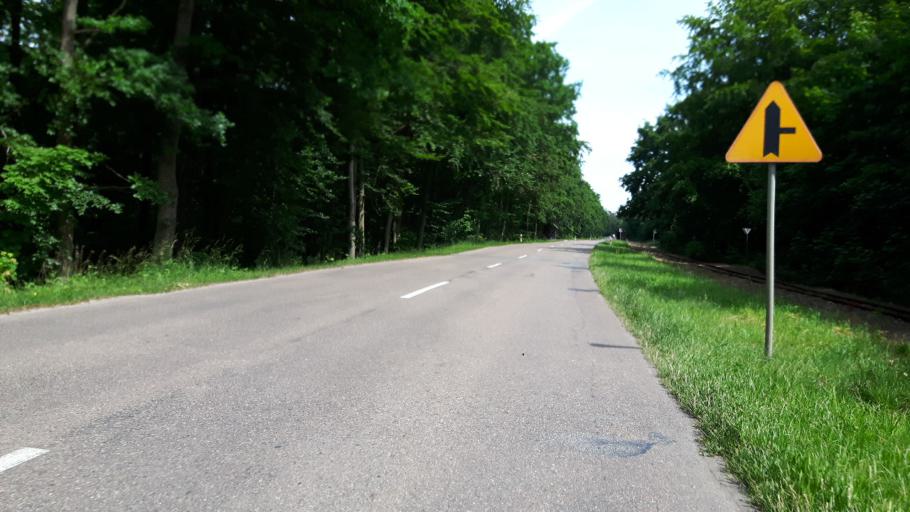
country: PL
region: Pomeranian Voivodeship
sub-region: Powiat nowodworski
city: Stegna
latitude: 54.3327
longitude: 19.0607
